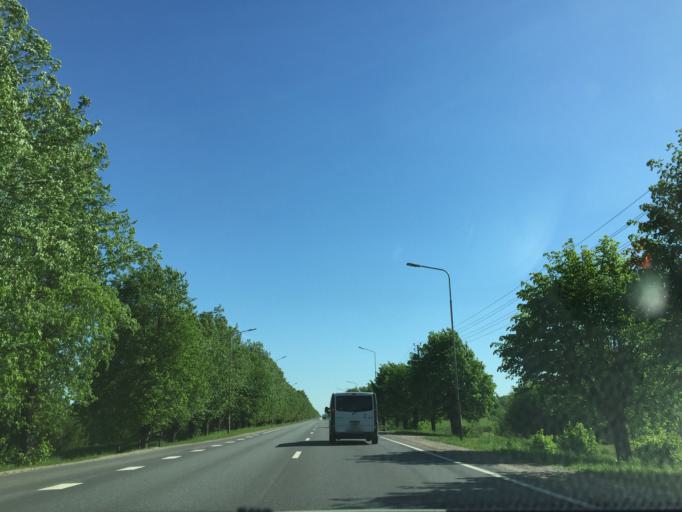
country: LV
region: Jelgava
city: Jelgava
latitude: 56.6197
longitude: 23.7236
